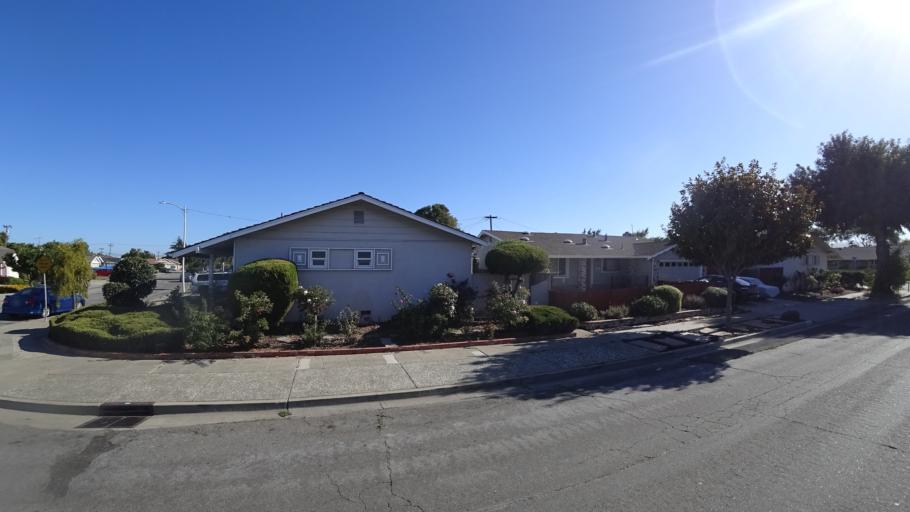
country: US
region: California
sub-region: Alameda County
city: Hayward
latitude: 37.6438
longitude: -122.1006
